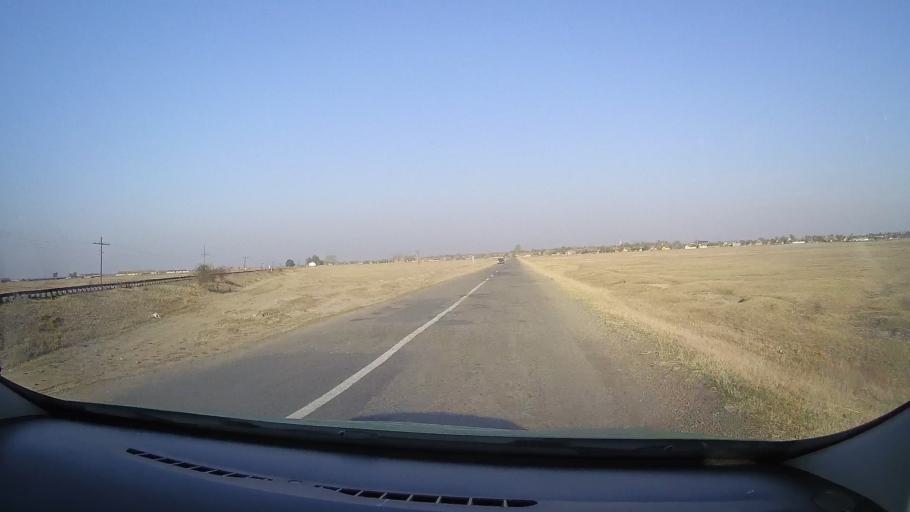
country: RO
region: Arad
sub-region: Comuna Graniceri
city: Graniceri
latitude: 46.5105
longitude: 21.3133
